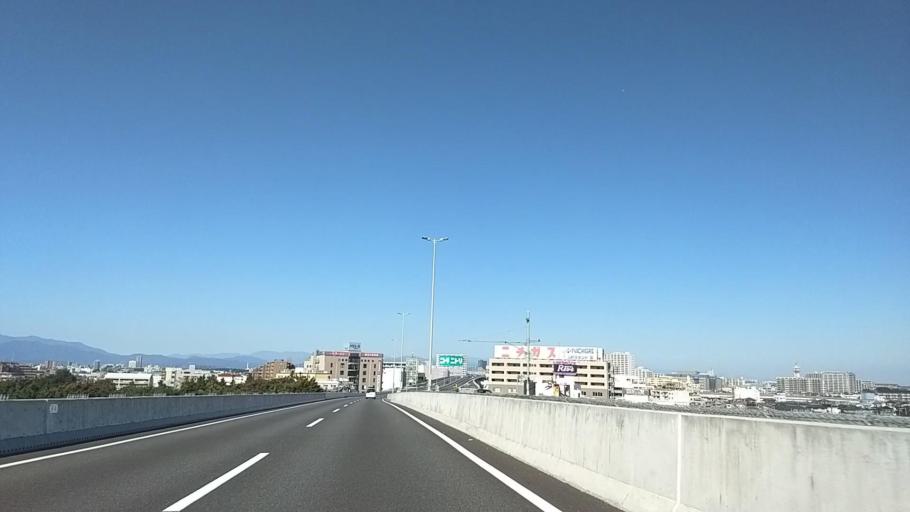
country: JP
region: Kanagawa
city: Minami-rinkan
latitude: 35.5059
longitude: 139.4815
